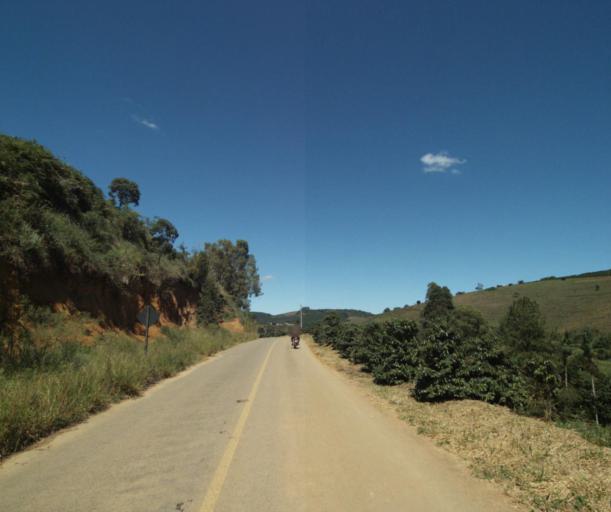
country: BR
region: Minas Gerais
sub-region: Espera Feliz
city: Espera Feliz
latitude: -20.5940
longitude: -41.8390
